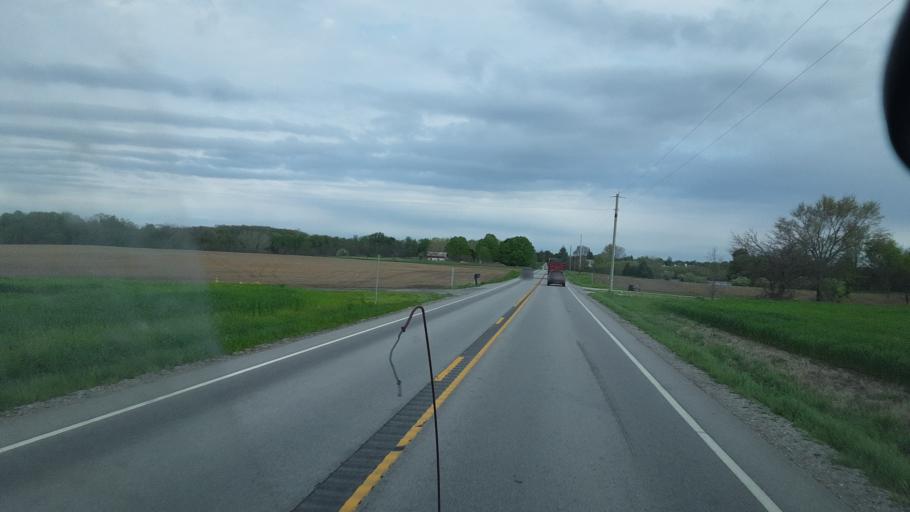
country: US
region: Indiana
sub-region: Whitley County
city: Tri-Lakes
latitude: 41.2771
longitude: -85.4181
